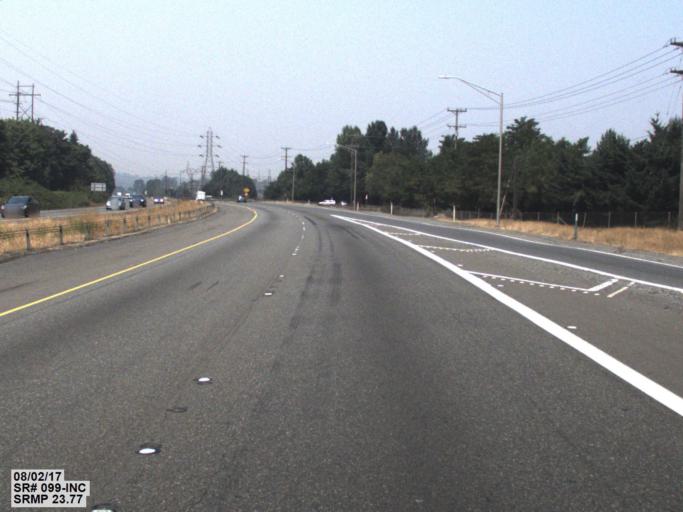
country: US
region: Washington
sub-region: King County
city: Boulevard Park
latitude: 47.5085
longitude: -122.3014
